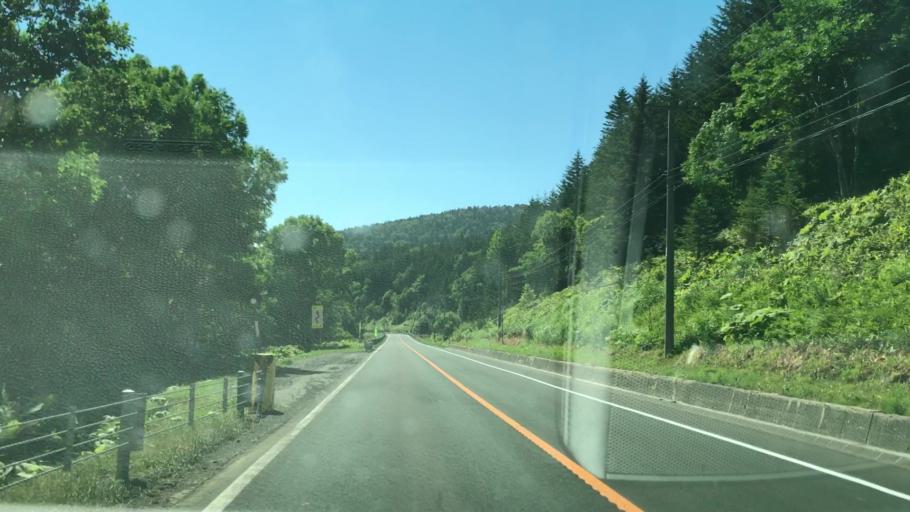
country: JP
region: Hokkaido
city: Shimo-furano
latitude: 42.9751
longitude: 142.6894
